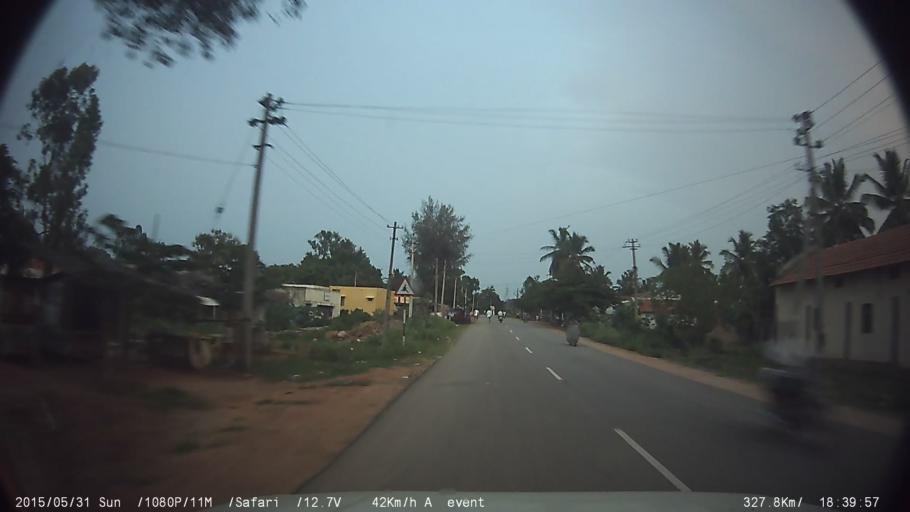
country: IN
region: Karnataka
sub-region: Mysore
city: Nanjangud
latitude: 12.1482
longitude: 76.7840
